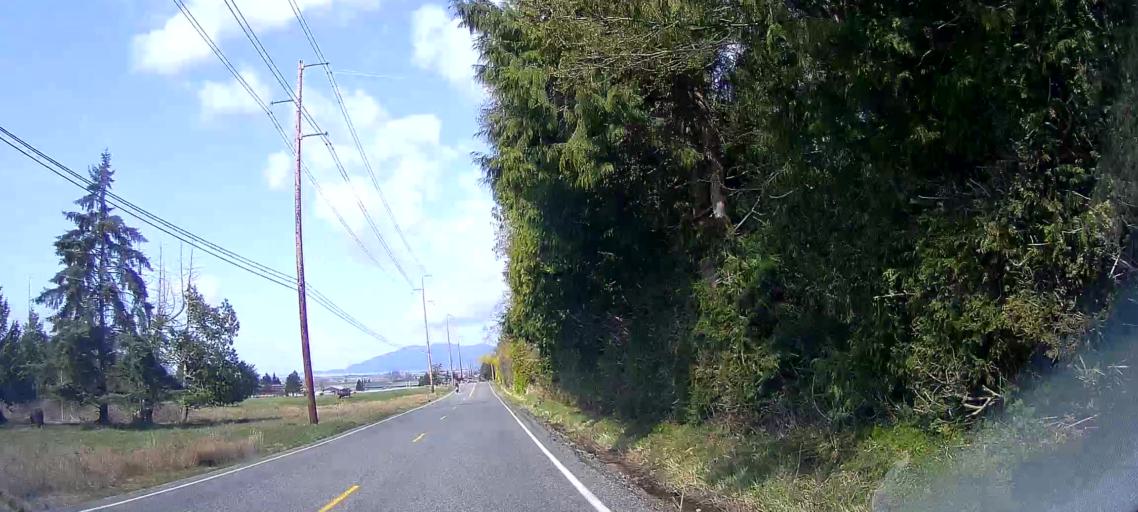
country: US
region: Washington
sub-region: Skagit County
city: Burlington
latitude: 48.5027
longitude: -122.4445
